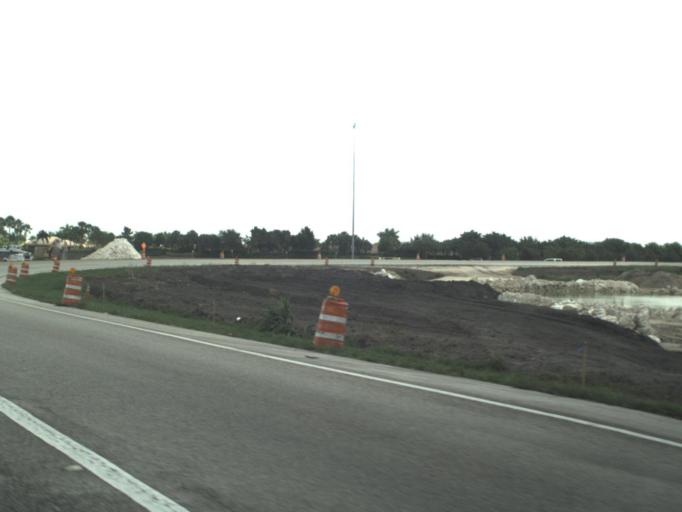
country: US
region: Florida
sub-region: Broward County
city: Southwest Ranches
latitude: 26.0633
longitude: -80.3537
